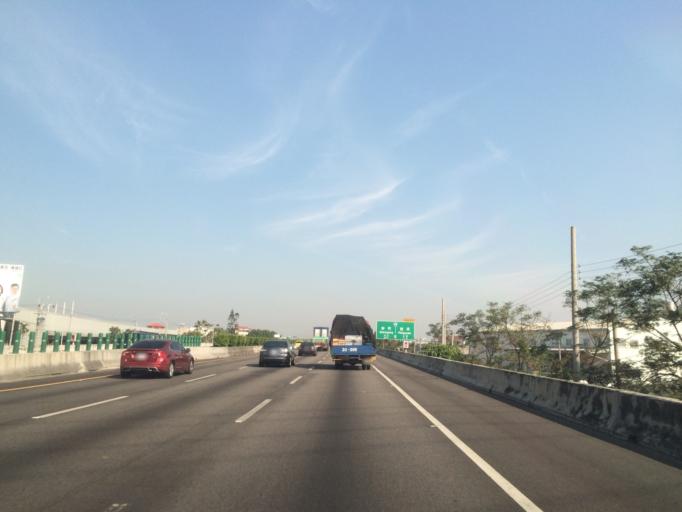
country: TW
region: Taiwan
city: Fengyuan
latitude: 24.2301
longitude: 120.6862
